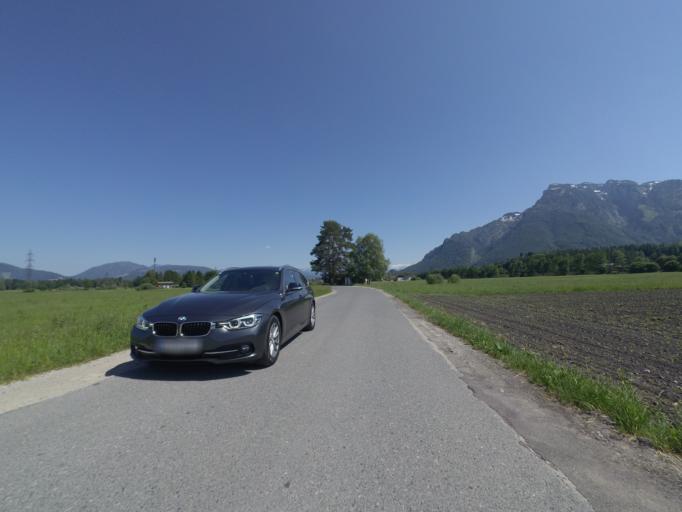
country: AT
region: Salzburg
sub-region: Politischer Bezirk Salzburg-Umgebung
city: Grodig
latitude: 47.7687
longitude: 12.9939
